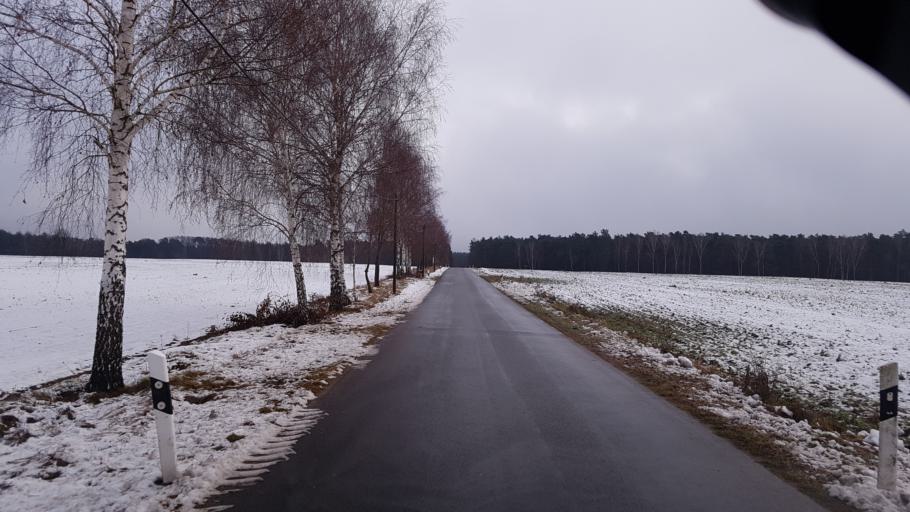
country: DE
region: Brandenburg
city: Straupitz
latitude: 51.9765
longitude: 14.1934
